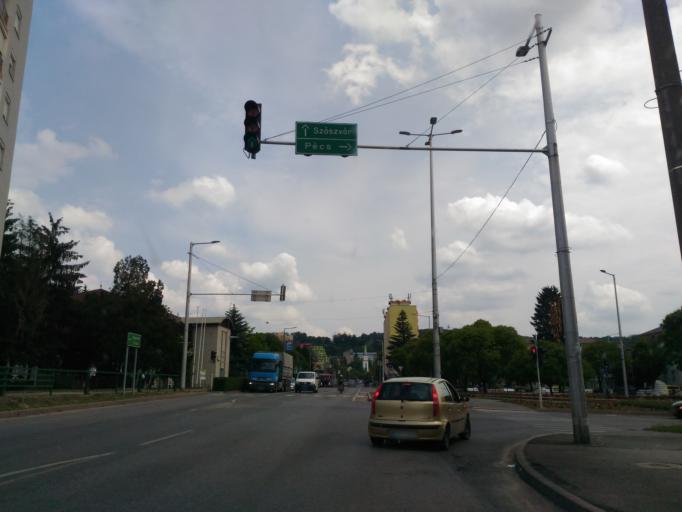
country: HU
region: Baranya
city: Komlo
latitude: 46.1914
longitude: 18.2609
